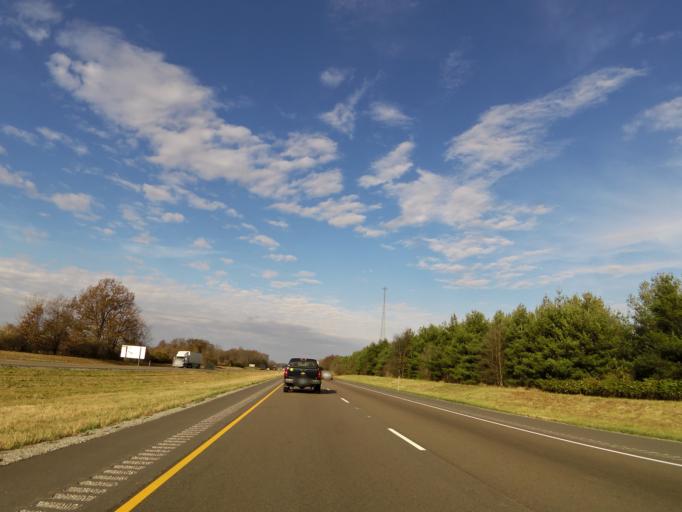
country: US
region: Illinois
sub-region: Washington County
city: Okawville
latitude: 38.4528
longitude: -89.5544
